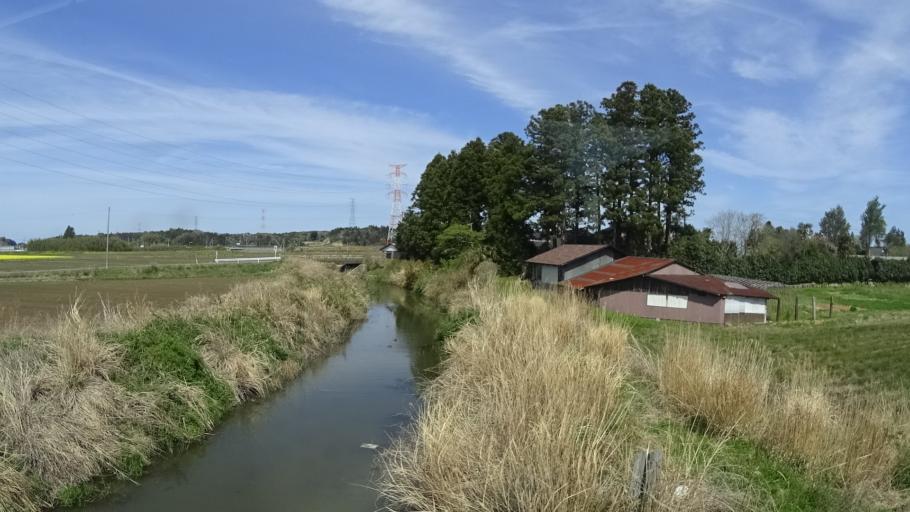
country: JP
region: Fukushima
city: Namie
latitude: 37.5942
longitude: 140.9988
